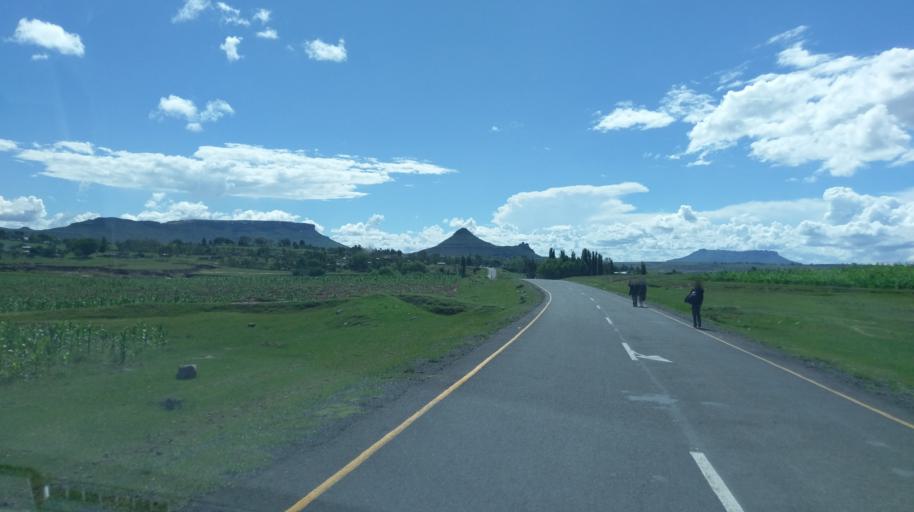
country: LS
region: Mafeteng
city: Mafeteng
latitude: -29.6960
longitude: 27.4485
